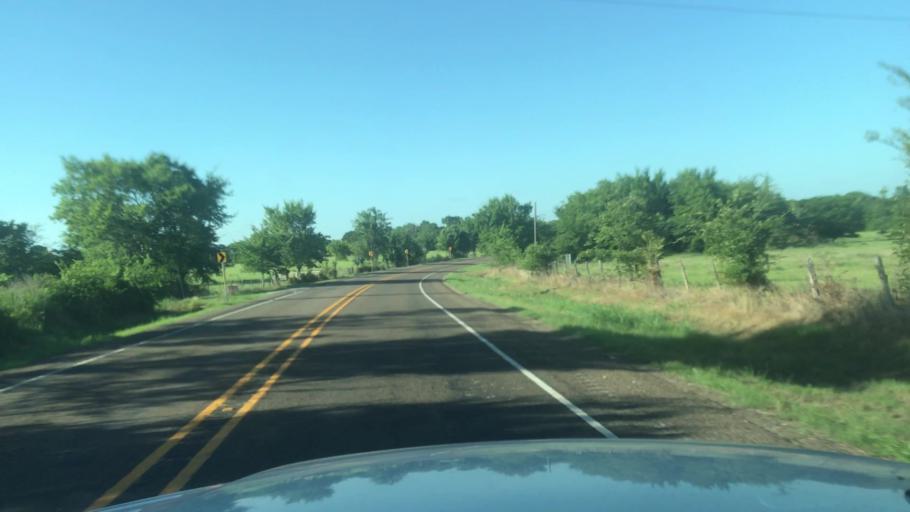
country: US
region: Texas
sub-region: Grimes County
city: Anderson
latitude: 30.6260
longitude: -95.8826
